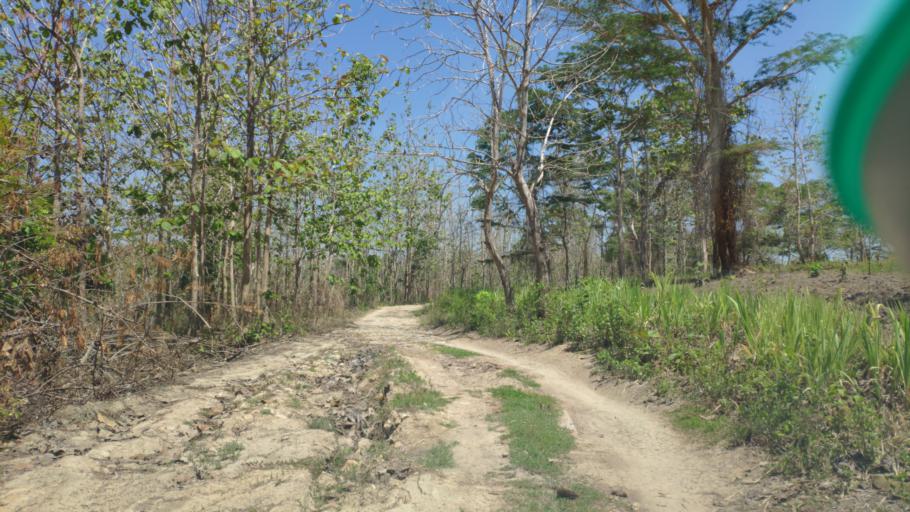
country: ID
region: Central Java
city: Suruhan
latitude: -7.0050
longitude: 111.5328
